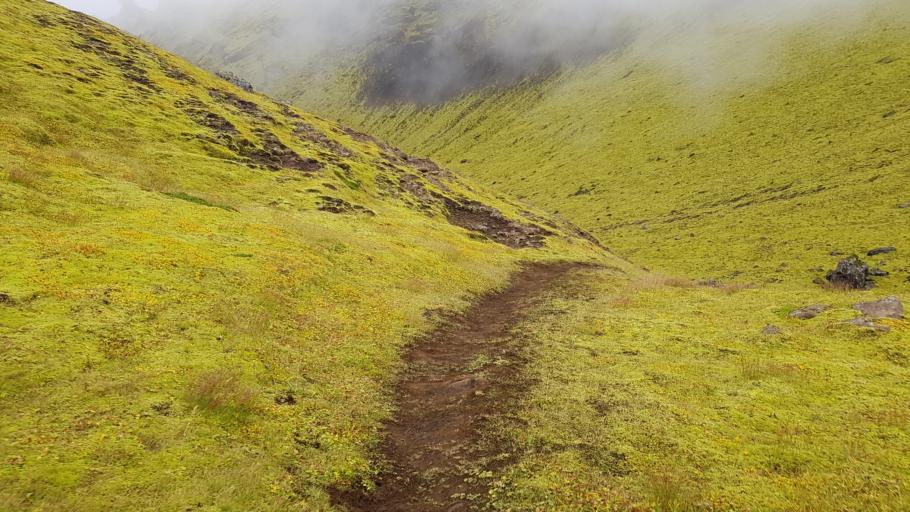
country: IS
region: South
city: Vestmannaeyjar
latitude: 63.5370
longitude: -18.8545
